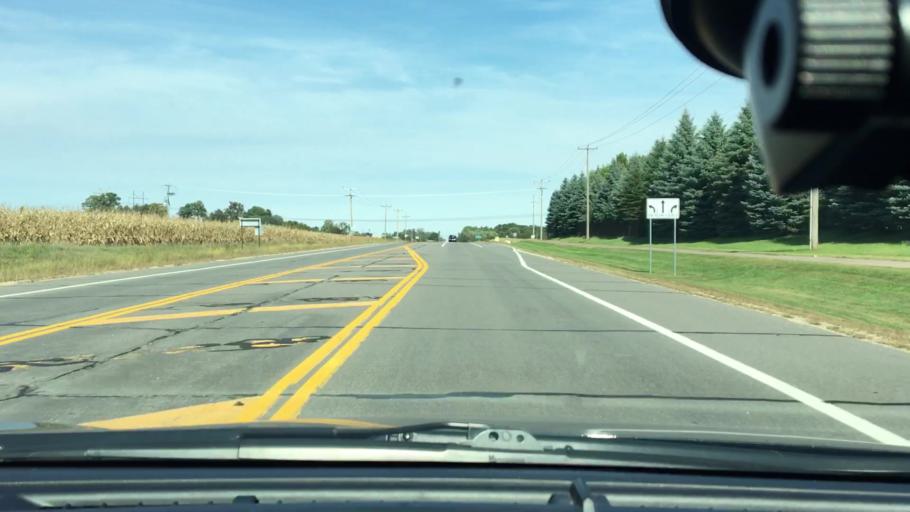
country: US
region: Minnesota
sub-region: Wright County
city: Hanover
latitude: 45.1724
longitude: -93.6657
